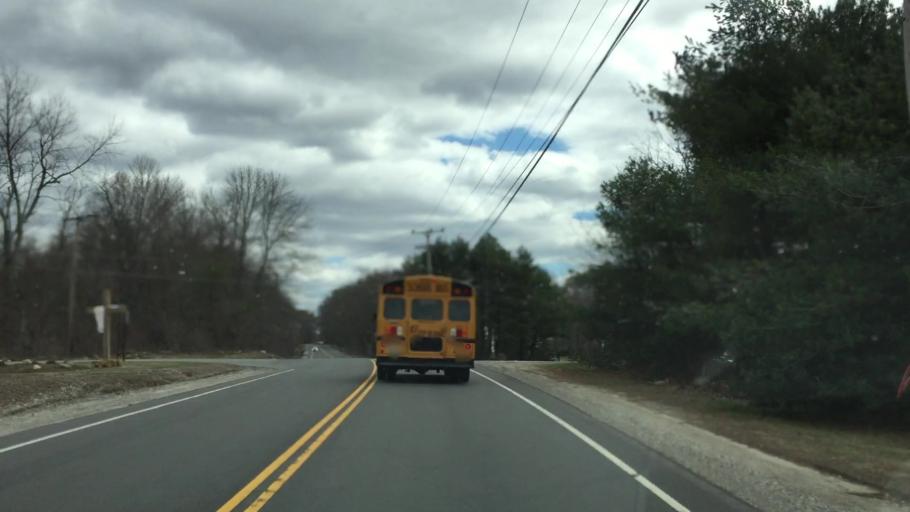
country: US
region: New Hampshire
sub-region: Rockingham County
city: Londonderry
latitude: 42.8217
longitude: -71.3634
